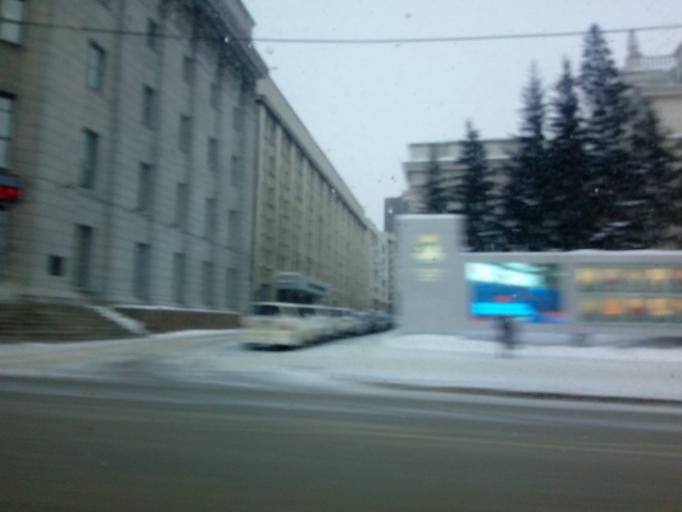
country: RU
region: Novosibirsk
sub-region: Novosibirskiy Rayon
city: Novosibirsk
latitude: 55.0282
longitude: 82.9211
